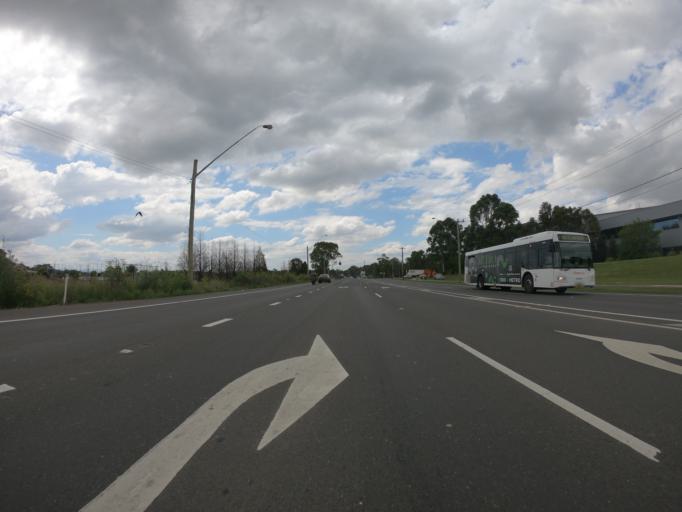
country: AU
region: New South Wales
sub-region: Blacktown
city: Mount Druitt
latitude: -33.8188
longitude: 150.7760
